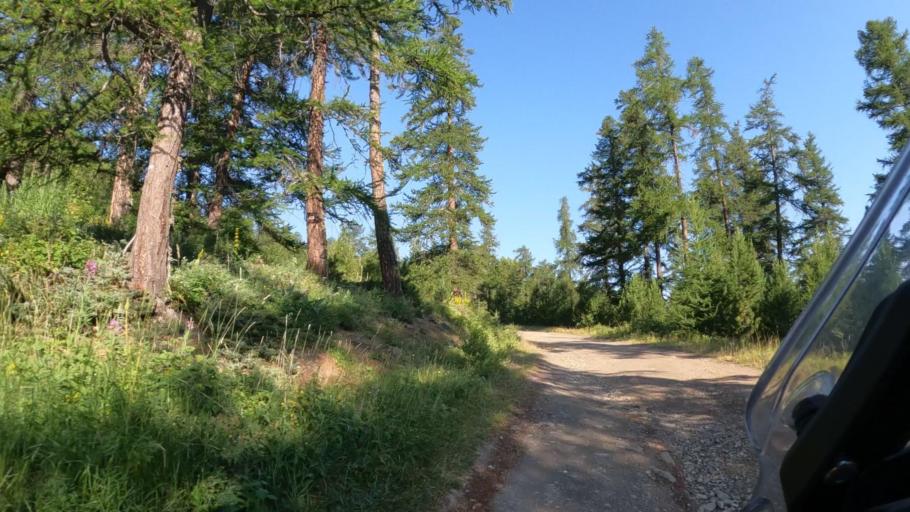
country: FR
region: Provence-Alpes-Cote d'Azur
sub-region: Departement des Hautes-Alpes
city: Guillestre
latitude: 44.6123
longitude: 6.6641
